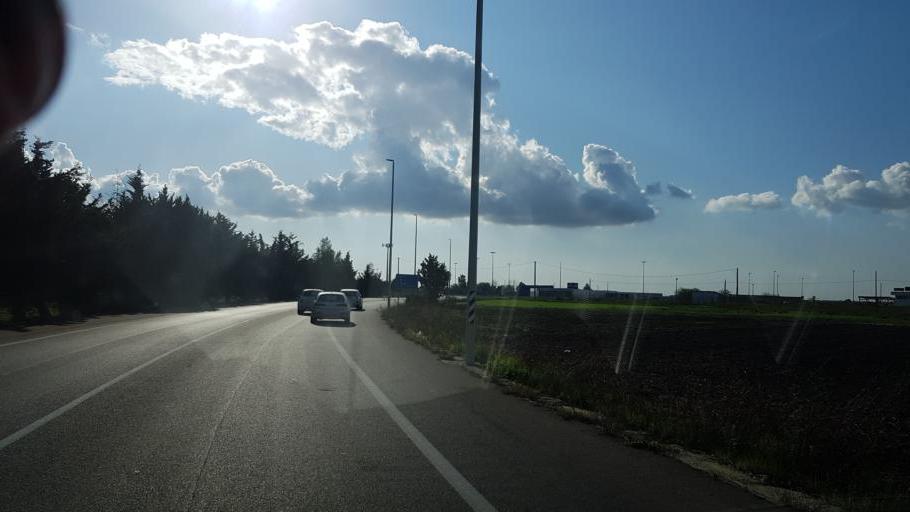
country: IT
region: Apulia
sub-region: Provincia di Lecce
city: Salice Salentino
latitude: 40.3760
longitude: 17.9691
